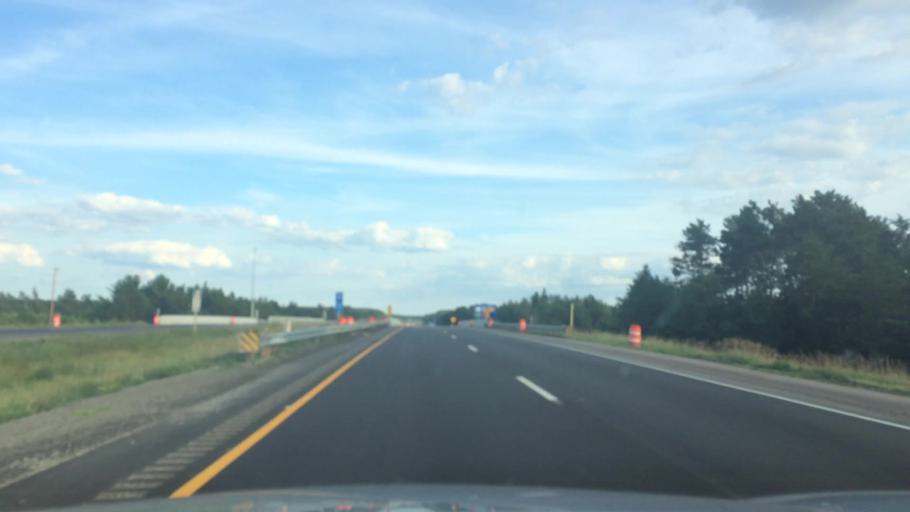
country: US
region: Wisconsin
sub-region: Portage County
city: Stevens Point
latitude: 44.5417
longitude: -89.5456
